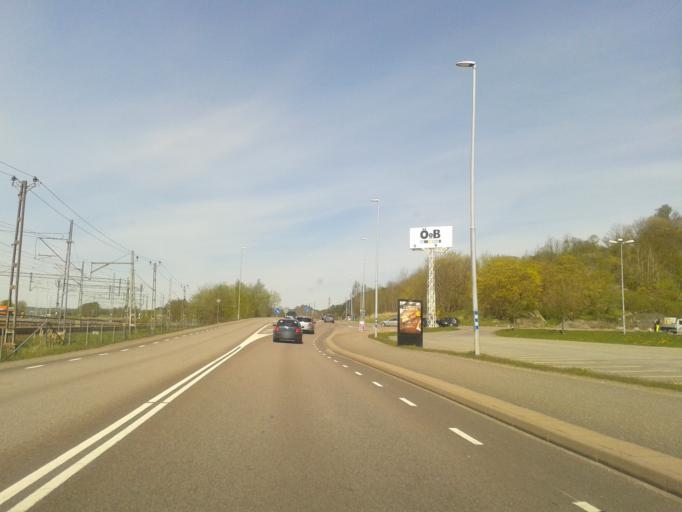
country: SE
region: Vaestra Goetaland
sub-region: Goteborg
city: Eriksbo
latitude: 57.7442
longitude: 12.0074
